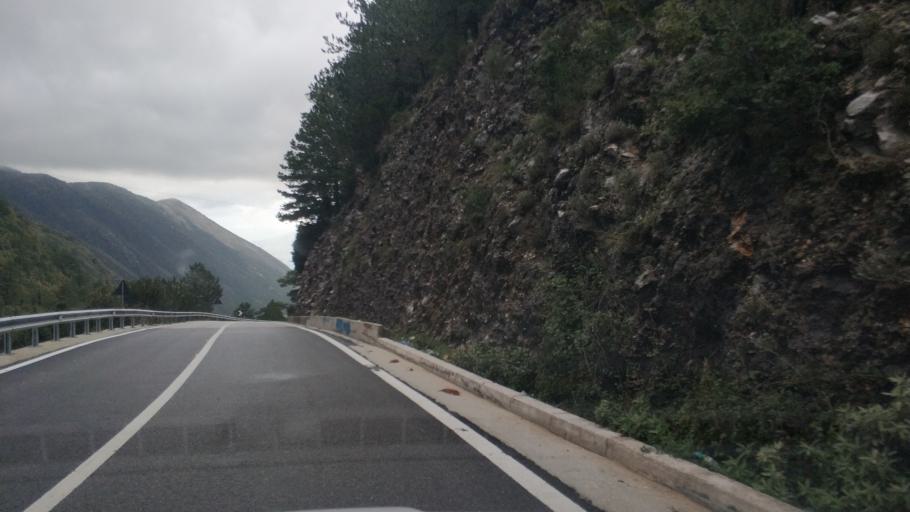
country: AL
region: Vlore
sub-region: Rrethi i Vlores
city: Brataj
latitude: 40.2192
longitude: 19.5795
